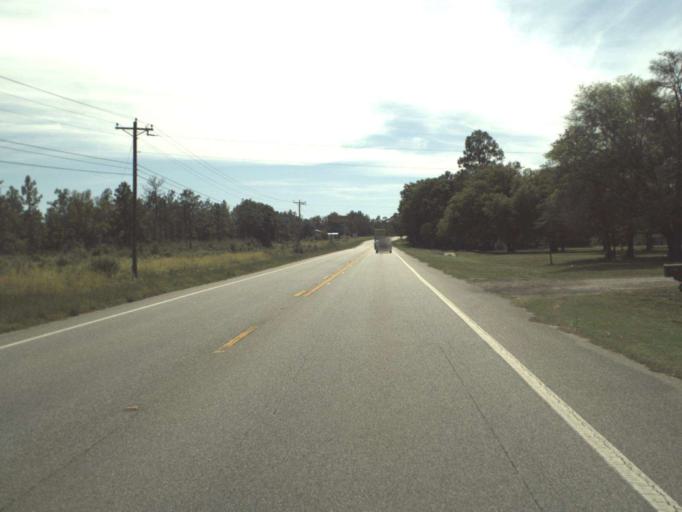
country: US
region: Florida
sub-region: Bay County
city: Lynn Haven
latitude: 30.4796
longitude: -85.6644
